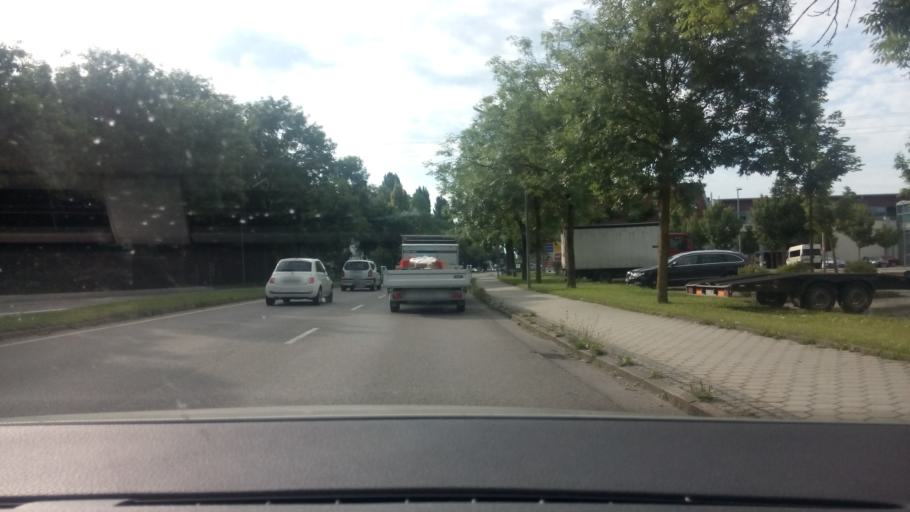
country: DE
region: Bavaria
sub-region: Upper Bavaria
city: Karlsfeld
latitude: 48.2282
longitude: 11.4631
